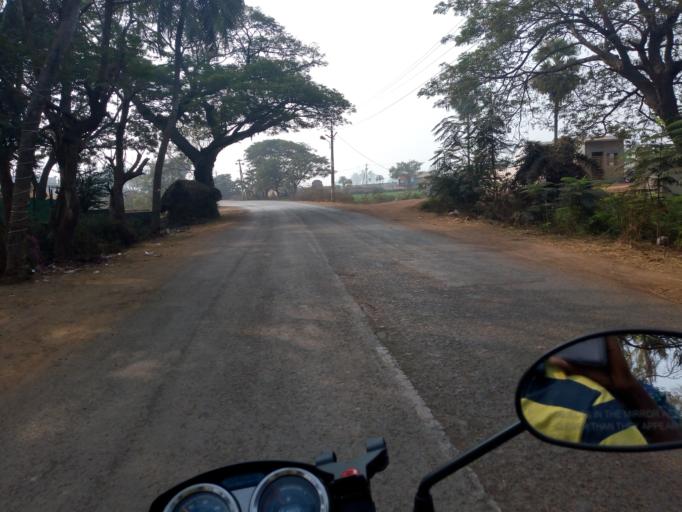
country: IN
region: Andhra Pradesh
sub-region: West Godavari
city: Tadepallegudem
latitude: 16.8094
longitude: 81.4084
